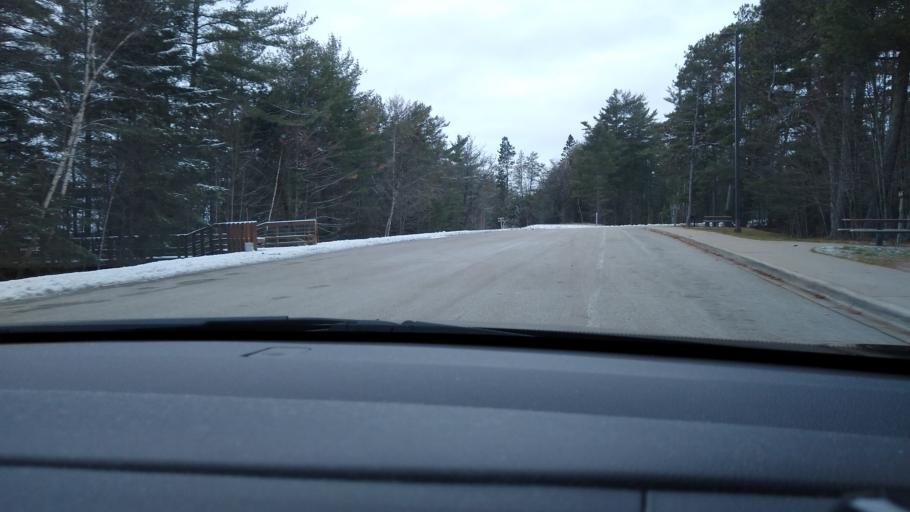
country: US
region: Michigan
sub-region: Luce County
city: Newberry
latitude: 46.0953
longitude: -85.3921
